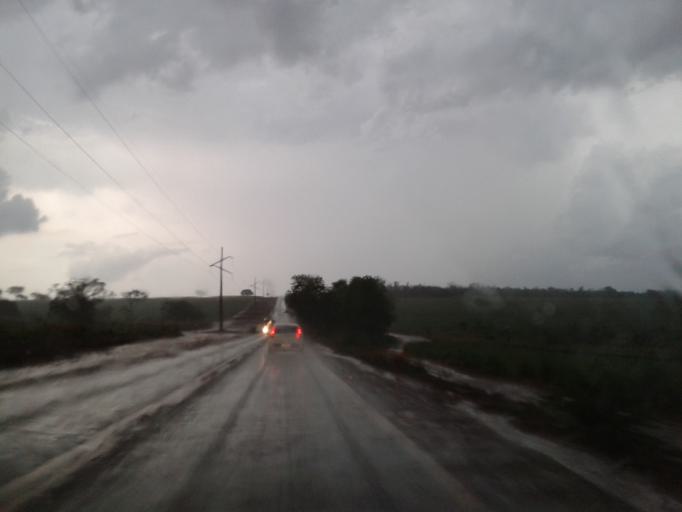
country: BR
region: Goias
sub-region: Quirinopolis
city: Quirinopolis
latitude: -18.5238
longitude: -50.4421
